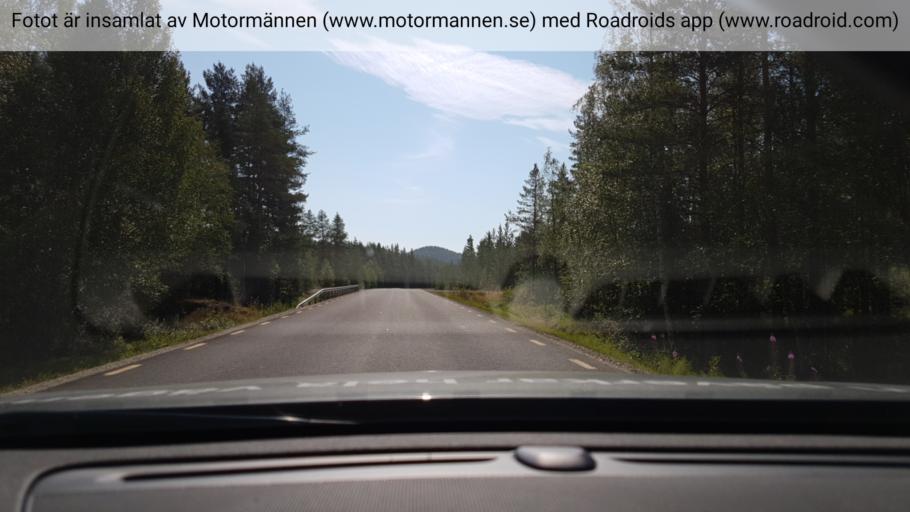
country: SE
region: Vaesterbotten
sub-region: Vindelns Kommun
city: Vindeln
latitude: 64.4639
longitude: 19.3270
